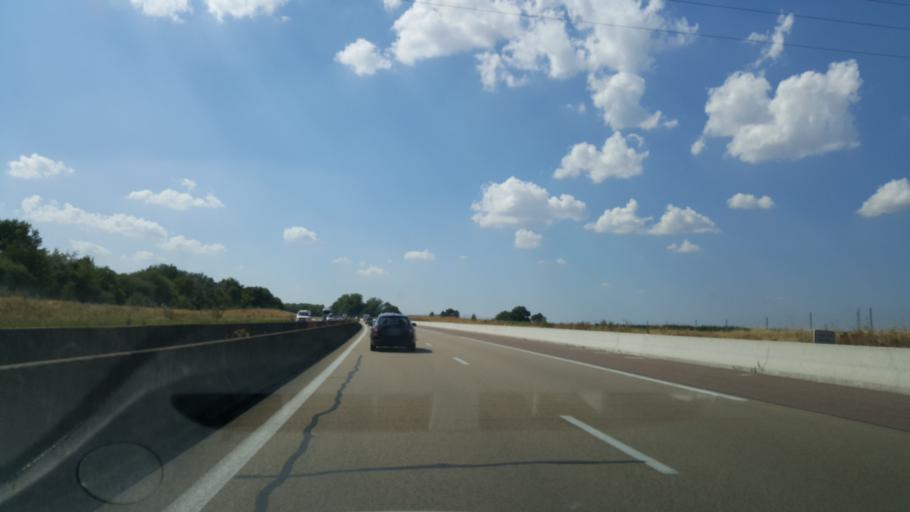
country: FR
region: Bourgogne
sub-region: Departement de l'Yonne
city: Avallon
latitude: 47.5057
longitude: 4.0884
